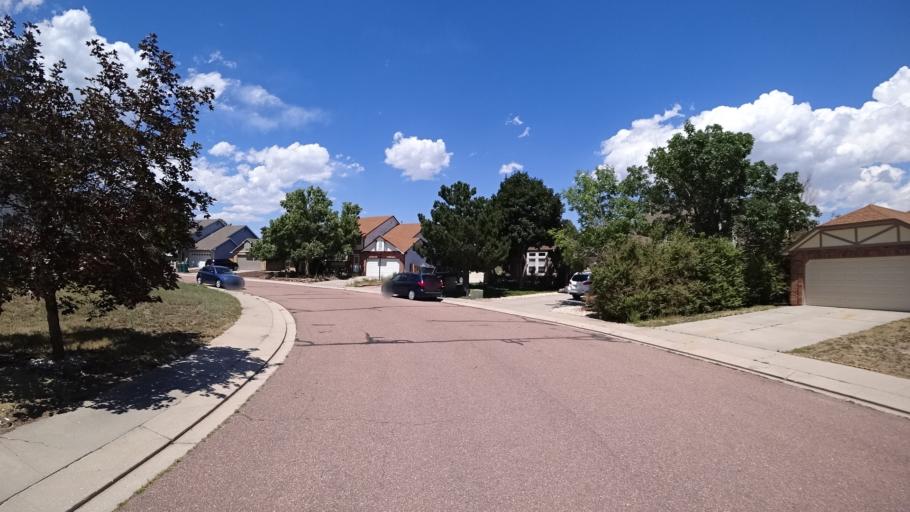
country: US
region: Colorado
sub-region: El Paso County
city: Black Forest
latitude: 38.9554
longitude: -104.7484
